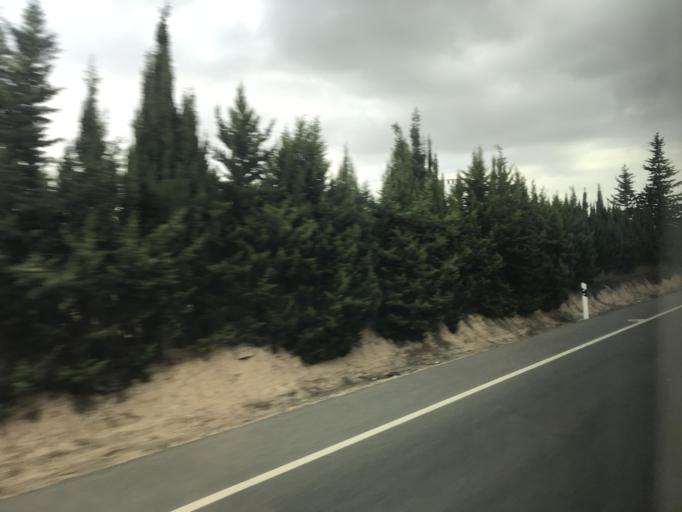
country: ES
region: Valencia
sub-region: Provincia de Alicante
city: Guardamar del Segura
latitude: 38.1267
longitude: -0.6510
